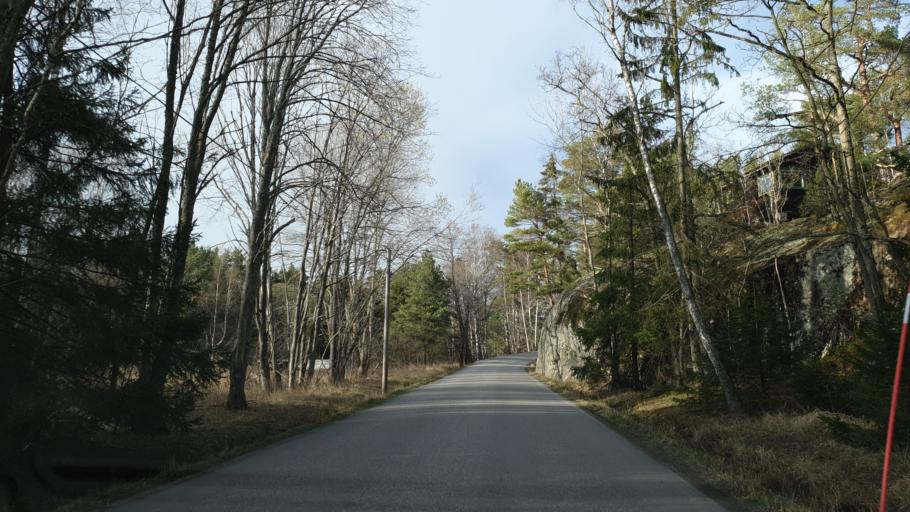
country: SE
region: Stockholm
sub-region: Varmdo Kommun
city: Holo
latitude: 59.3627
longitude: 18.6705
